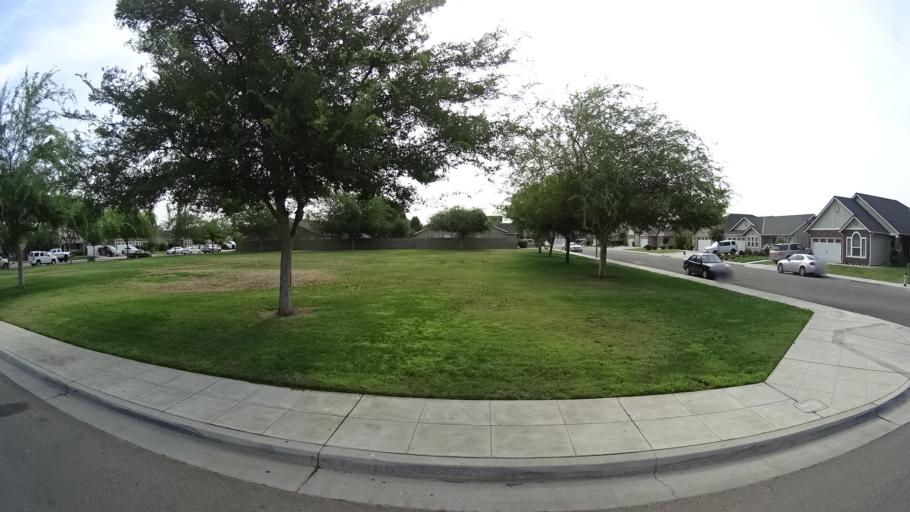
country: US
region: California
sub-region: Fresno County
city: West Park
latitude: 36.7735
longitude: -119.8785
